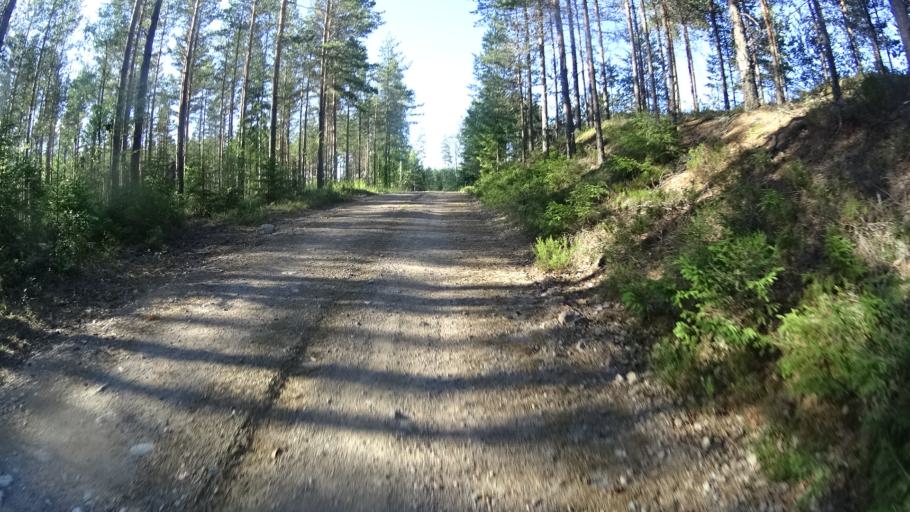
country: FI
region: Uusimaa
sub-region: Helsinki
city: Karkkila
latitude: 60.6556
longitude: 24.1326
